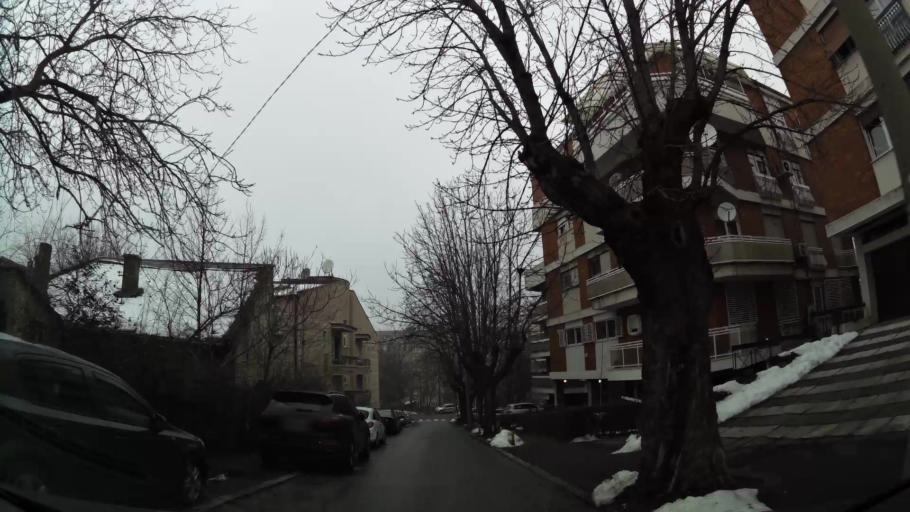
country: RS
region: Central Serbia
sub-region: Belgrade
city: Savski Venac
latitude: 44.7939
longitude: 20.4406
